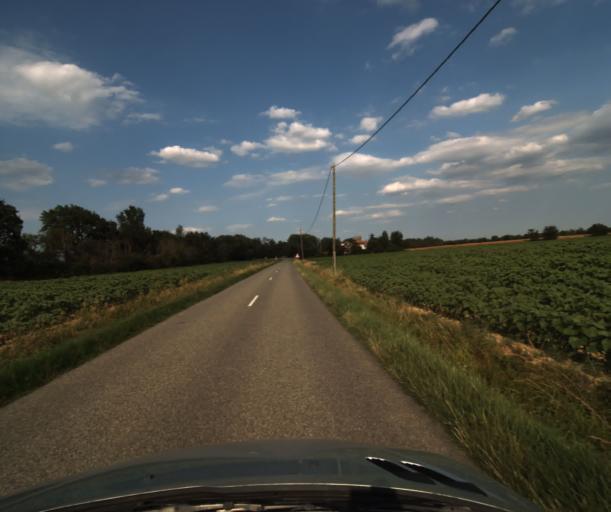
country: FR
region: Midi-Pyrenees
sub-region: Departement de la Haute-Garonne
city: Fonsorbes
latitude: 43.5159
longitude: 1.2253
